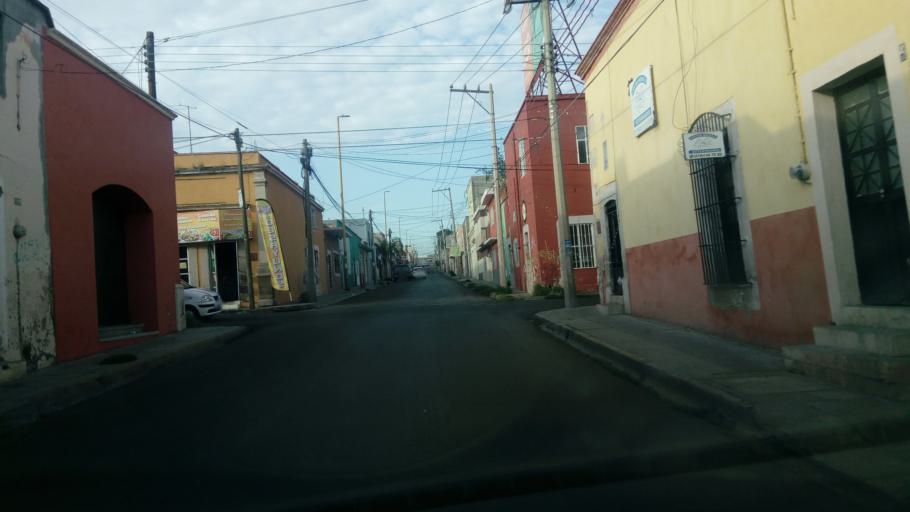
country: MX
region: Durango
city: Victoria de Durango
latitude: 24.0186
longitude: -104.6754
